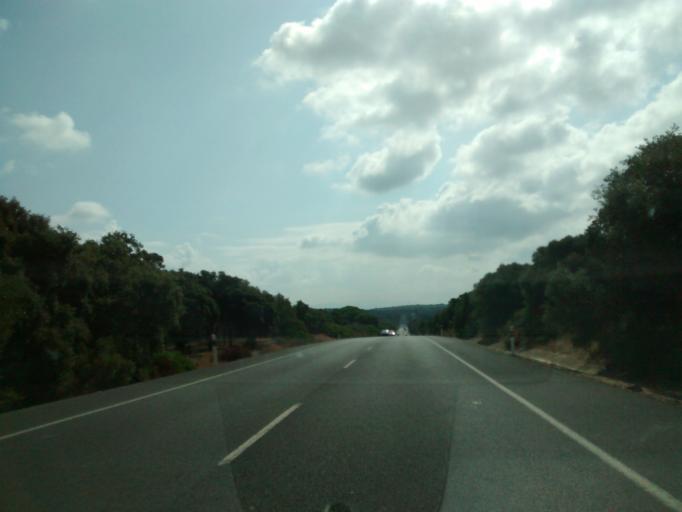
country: ES
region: Andalusia
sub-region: Provincia de Cadiz
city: Vejer de la Frontera
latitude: 36.2525
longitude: -5.9338
